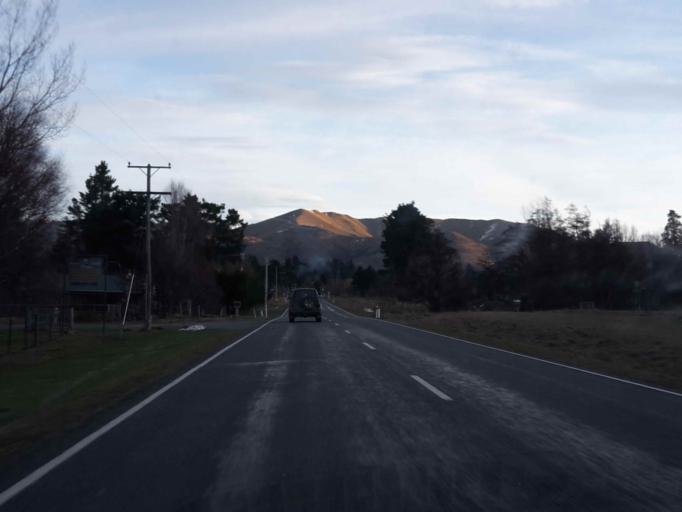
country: NZ
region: Canterbury
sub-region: Timaru District
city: Pleasant Point
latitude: -44.0849
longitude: 170.6579
